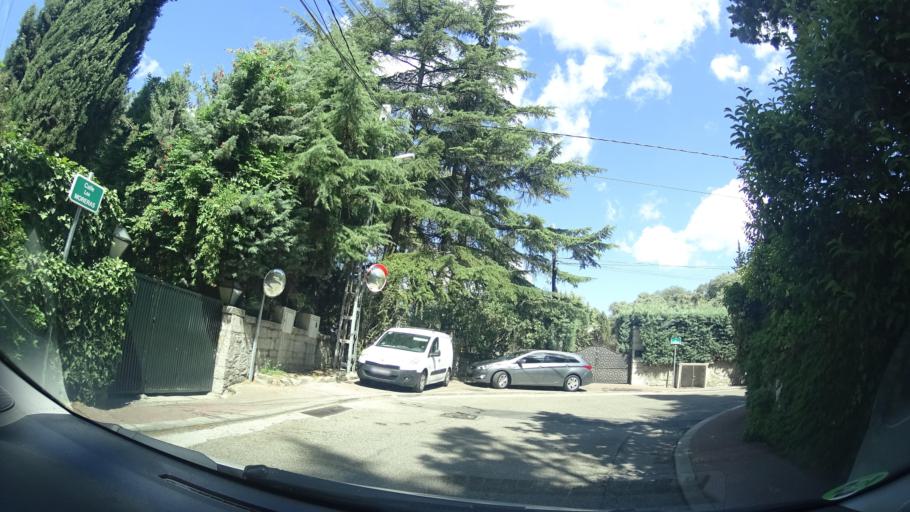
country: ES
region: Madrid
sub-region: Provincia de Madrid
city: Collado-Villalba
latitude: 40.6249
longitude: -3.9954
